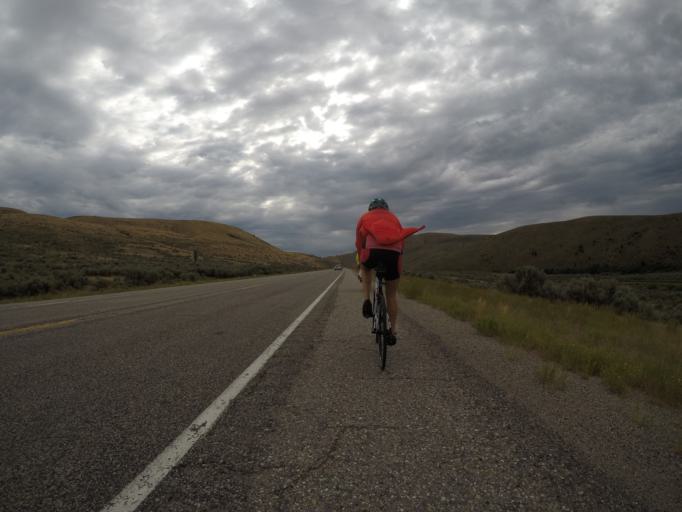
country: US
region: Wyoming
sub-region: Lincoln County
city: Kemmerer
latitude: 41.8229
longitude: -110.8665
